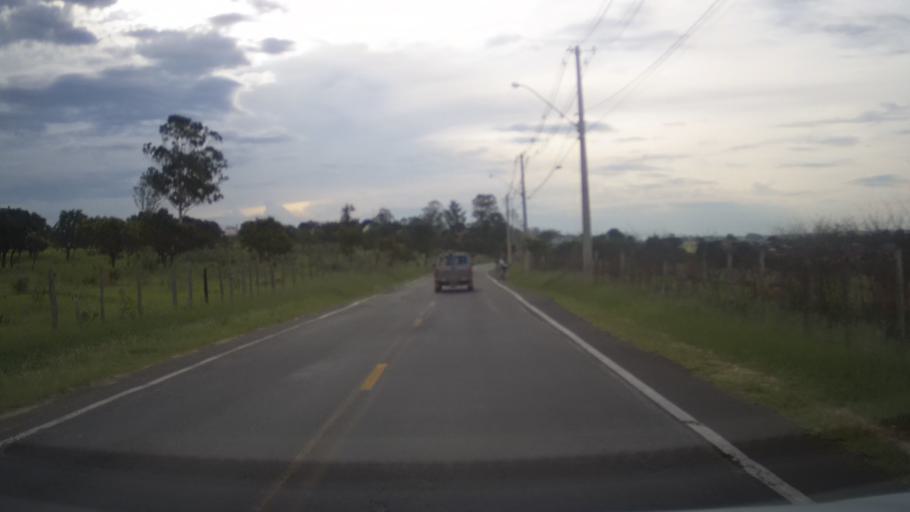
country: BR
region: Sao Paulo
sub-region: Hortolandia
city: Hortolandia
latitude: -22.9572
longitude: -47.2111
